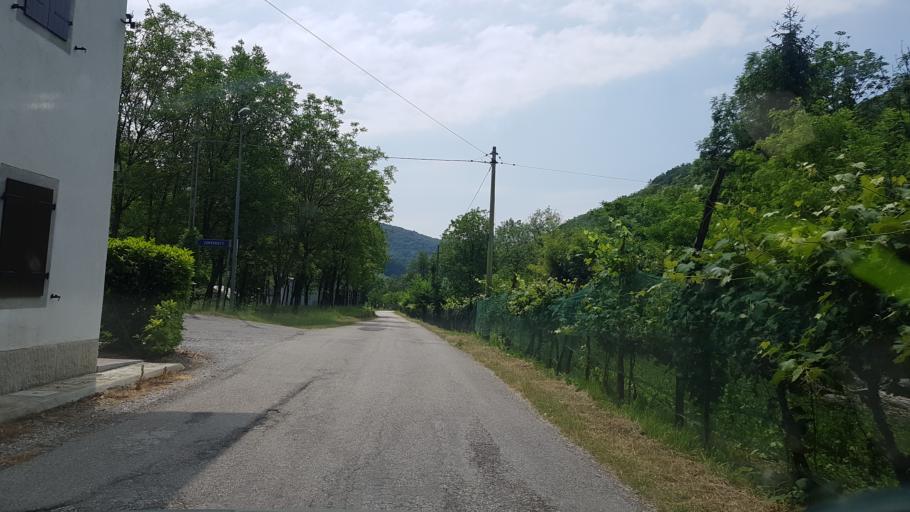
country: IT
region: Friuli Venezia Giulia
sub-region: Provincia di Udine
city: Torreano
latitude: 46.1503
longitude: 13.4377
